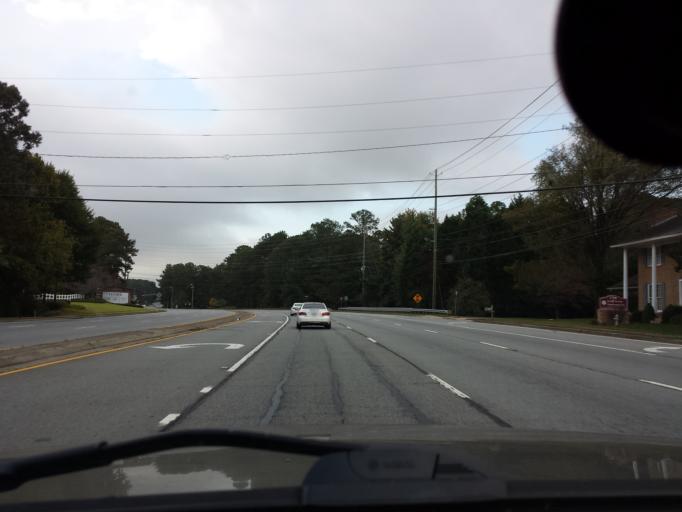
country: US
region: Georgia
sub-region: Fulton County
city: Roswell
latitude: 34.0601
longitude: -84.4149
